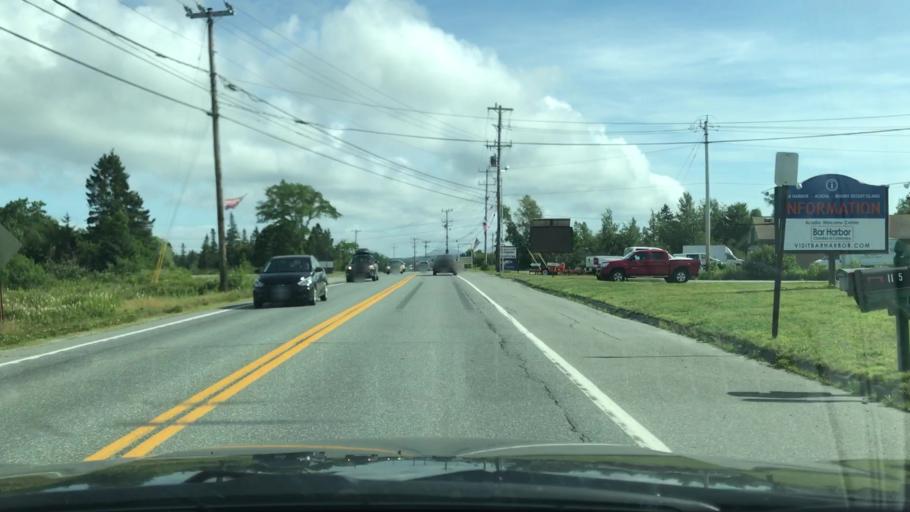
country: US
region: Maine
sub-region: Hancock County
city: Trenton
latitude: 44.4351
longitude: -68.3690
